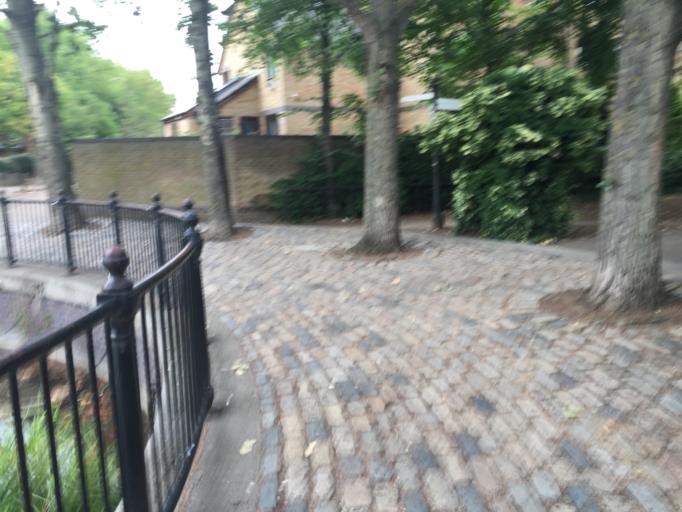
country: GB
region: England
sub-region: Greater London
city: Bethnal Green
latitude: 51.5027
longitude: -0.0455
